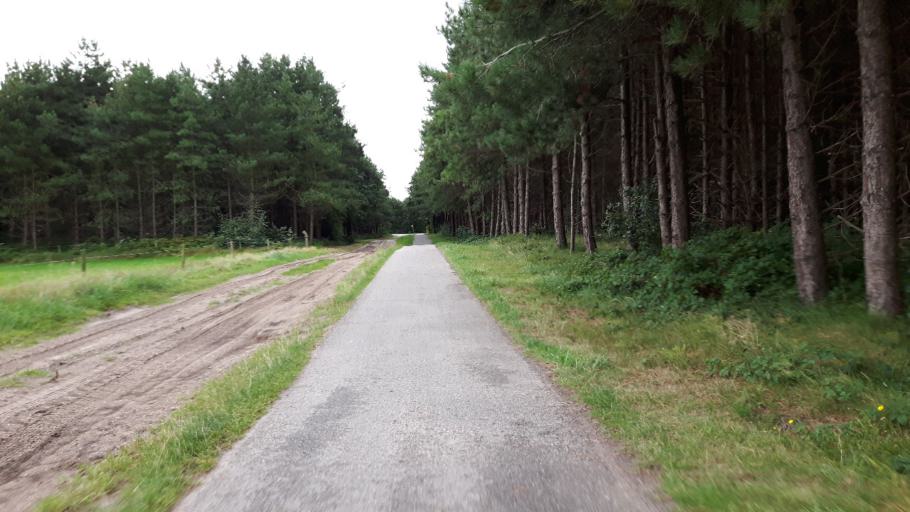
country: NL
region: Friesland
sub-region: Gemeente Ameland
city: Nes
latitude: 53.4477
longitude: 5.7126
